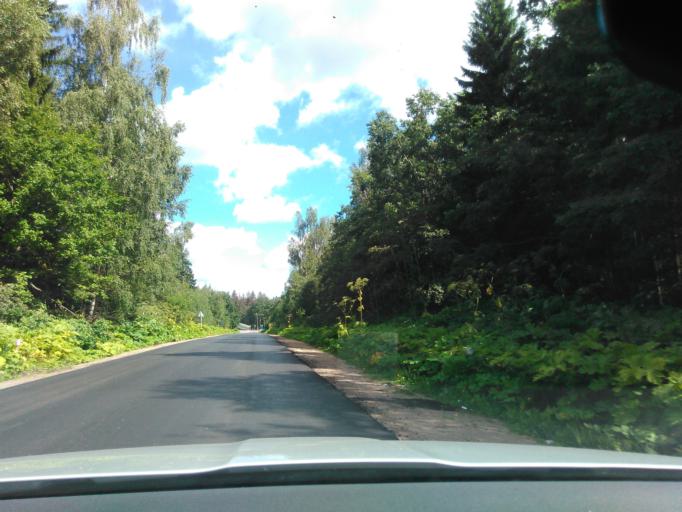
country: RU
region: Moskovskaya
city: Klin
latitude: 56.2705
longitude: 36.8367
